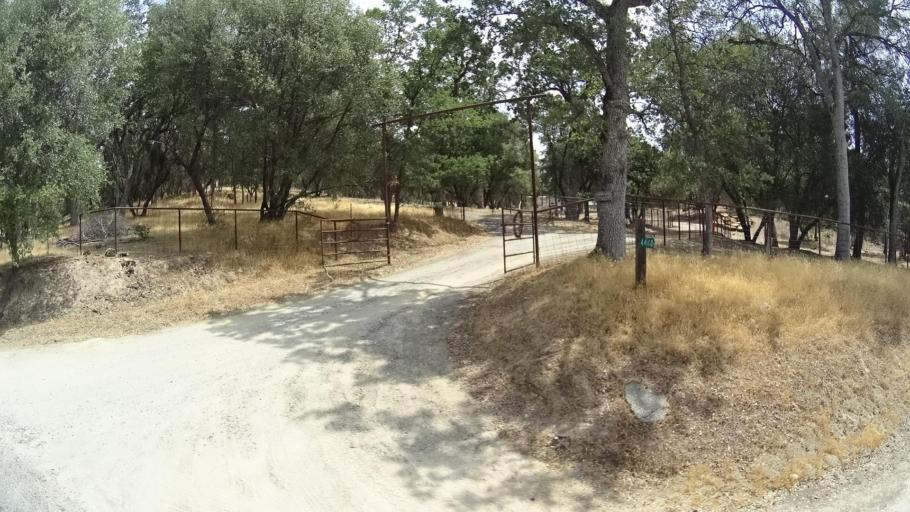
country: US
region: California
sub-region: Madera County
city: Ahwahnee
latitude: 37.4262
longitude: -119.8181
